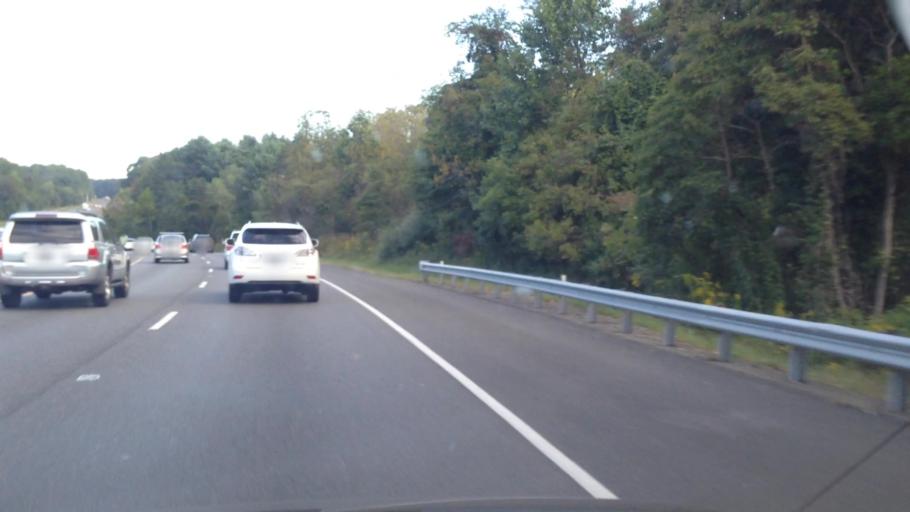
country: US
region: Virginia
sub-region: Fairfax County
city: Fairfax Station
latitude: 38.8132
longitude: -77.3435
